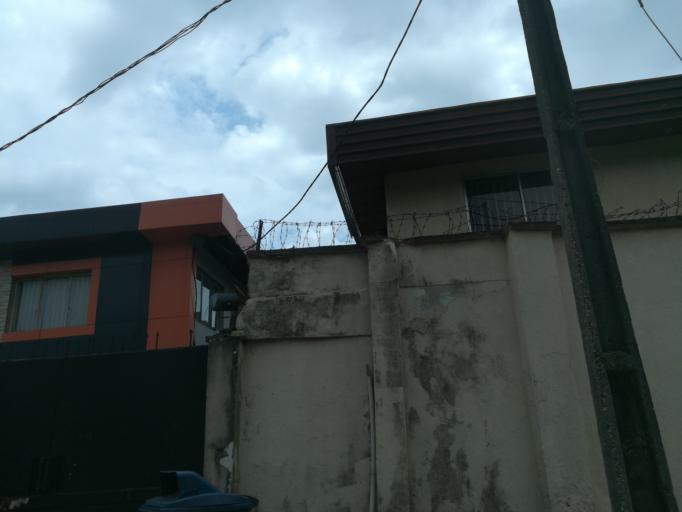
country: NG
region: Lagos
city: Ikeja
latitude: 6.5928
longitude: 3.3558
